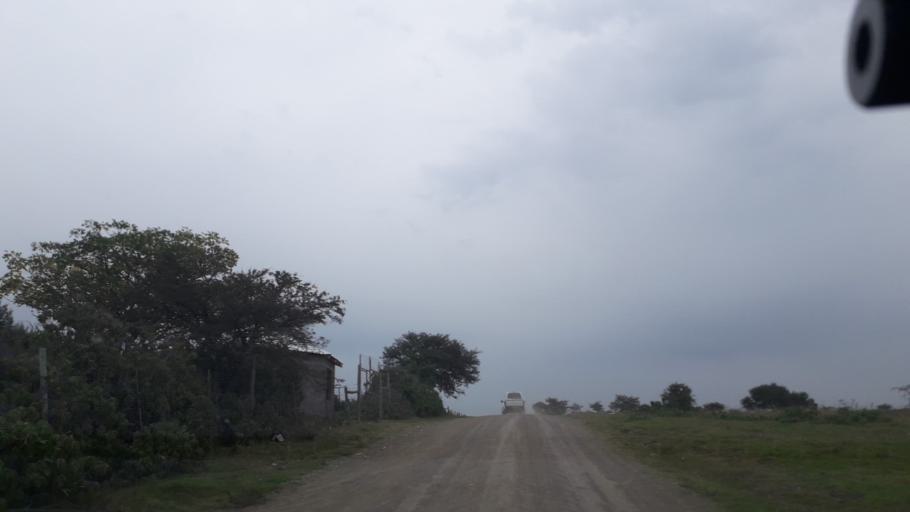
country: ZA
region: Eastern Cape
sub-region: Buffalo City Metropolitan Municipality
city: Bhisho
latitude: -32.7958
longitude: 27.3408
